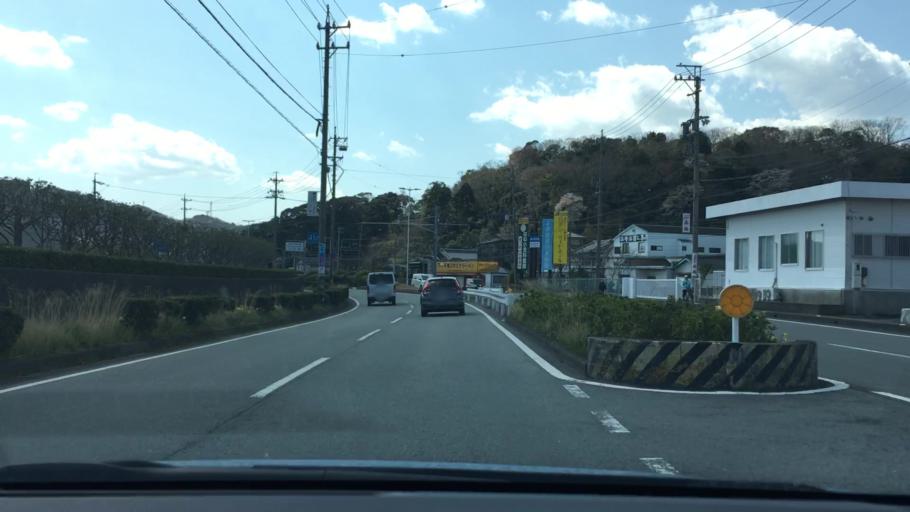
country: JP
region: Mie
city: Toba
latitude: 34.4749
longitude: 136.8454
